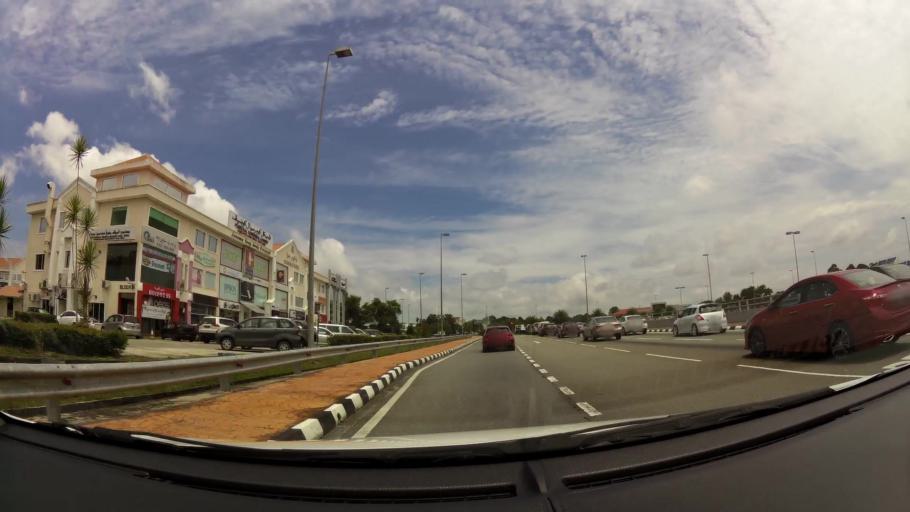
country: BN
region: Brunei and Muara
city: Bandar Seri Begawan
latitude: 4.9023
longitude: 114.9200
